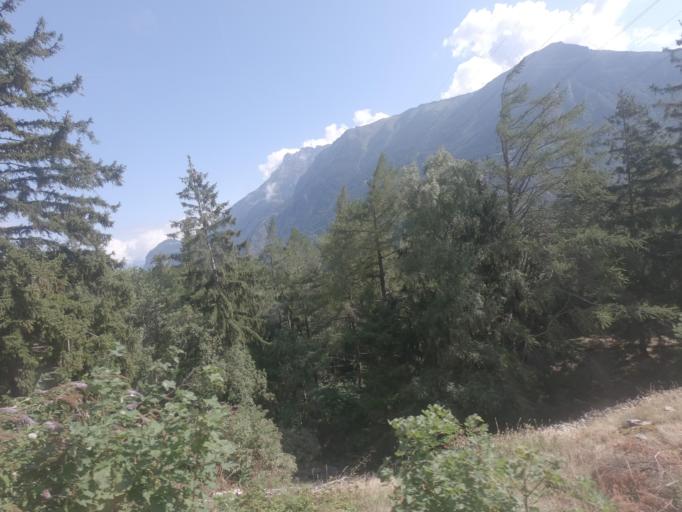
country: CH
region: Valais
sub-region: Saint-Maurice District
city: Vernayaz
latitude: 46.1291
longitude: 7.0334
